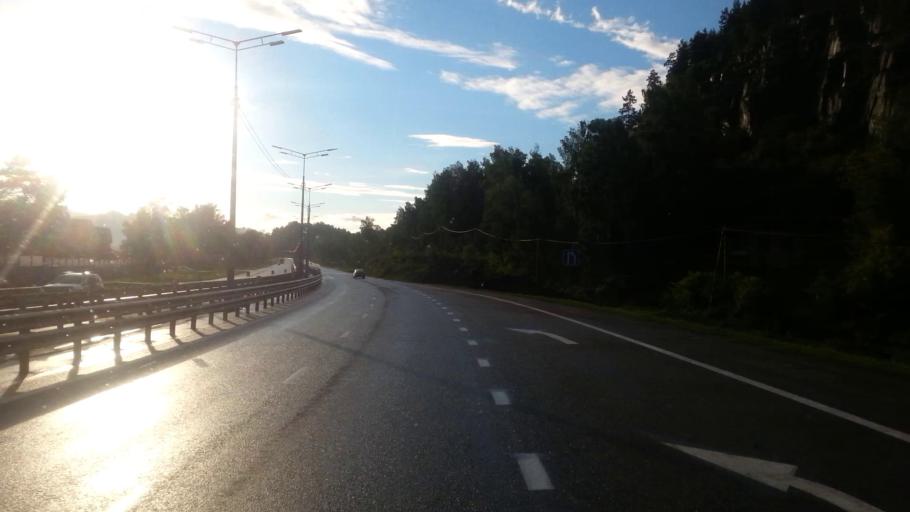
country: RU
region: Altay
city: Souzga
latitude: 51.9192
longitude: 85.8574
